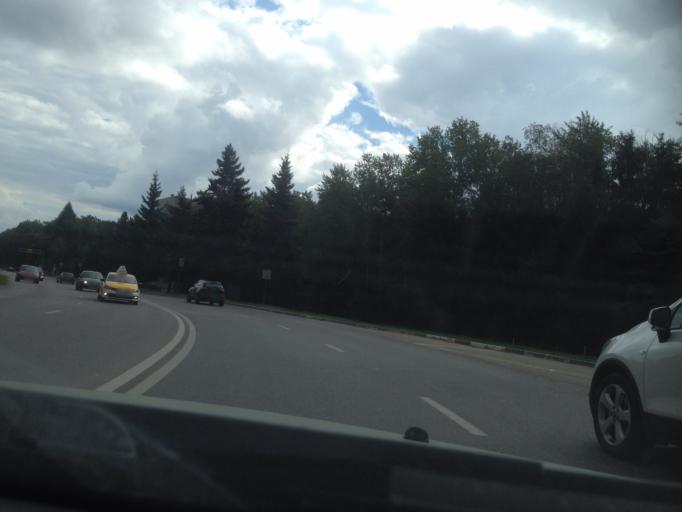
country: RU
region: Voronezj
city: Podgornoye
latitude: 51.7260
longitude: 39.1981
